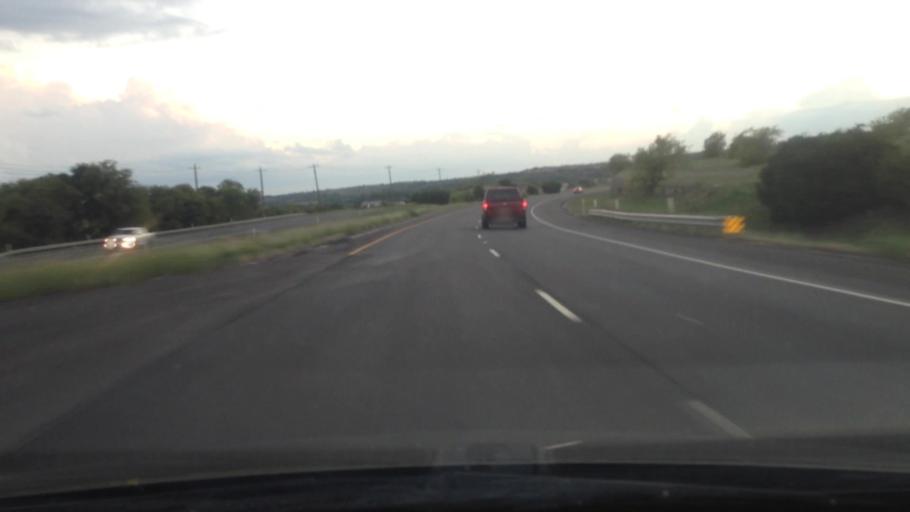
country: US
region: Texas
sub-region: Hood County
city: DeCordova
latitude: 32.5128
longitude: -97.6337
